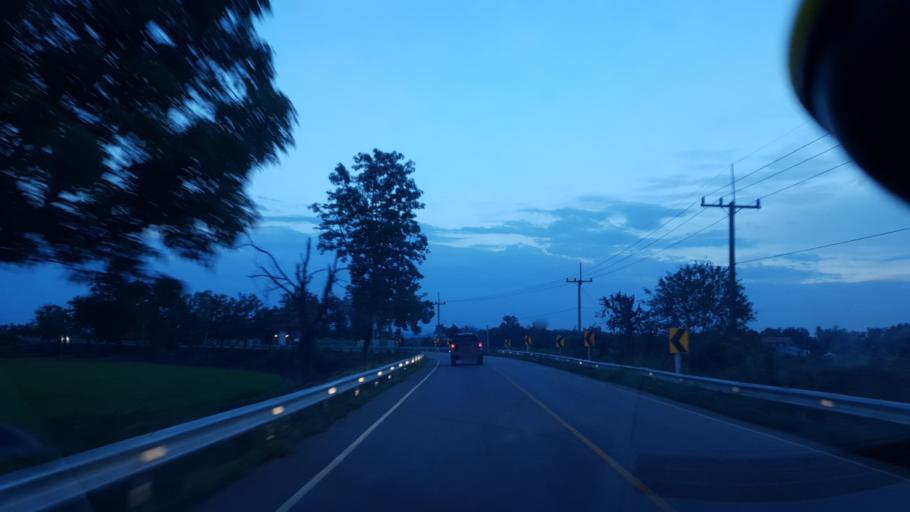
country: TH
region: Chiang Rai
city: Wiang Chiang Rung
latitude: 19.9681
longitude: 99.9812
